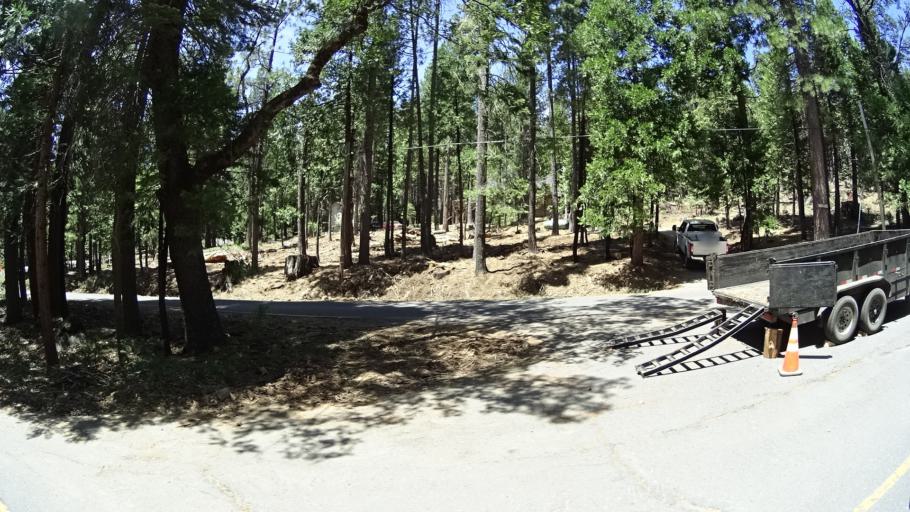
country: US
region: California
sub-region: Calaveras County
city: Arnold
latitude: 38.3040
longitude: -120.2628
